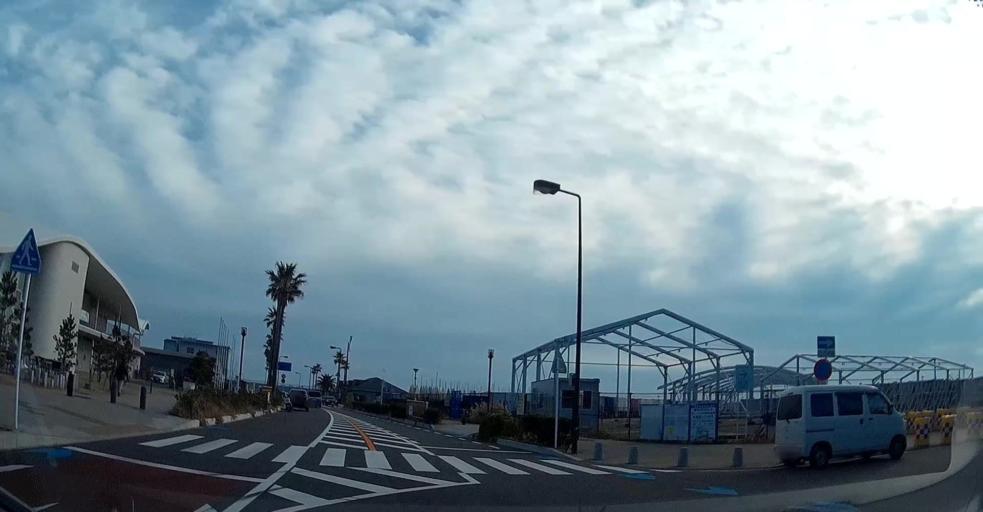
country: JP
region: Kanagawa
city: Fujisawa
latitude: 35.2998
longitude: 139.4829
